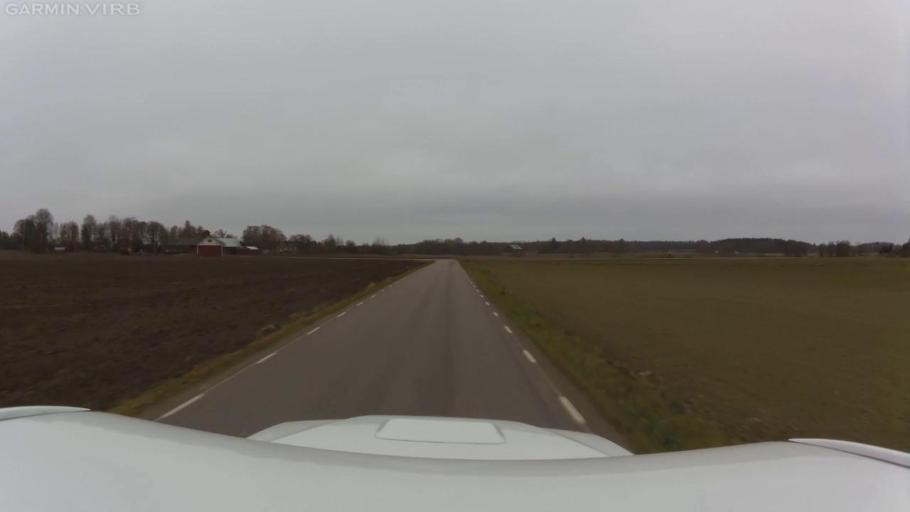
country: SE
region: OEstergoetland
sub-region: Linkopings Kommun
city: Vikingstad
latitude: 58.3232
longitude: 15.3790
